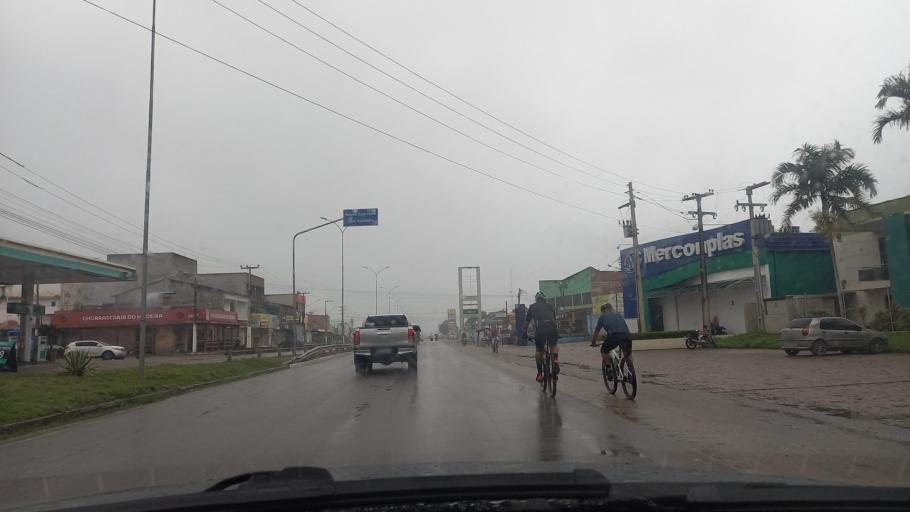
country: BR
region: Alagoas
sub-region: Arapiraca
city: Arapiraca
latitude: -9.7237
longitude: -36.6807
